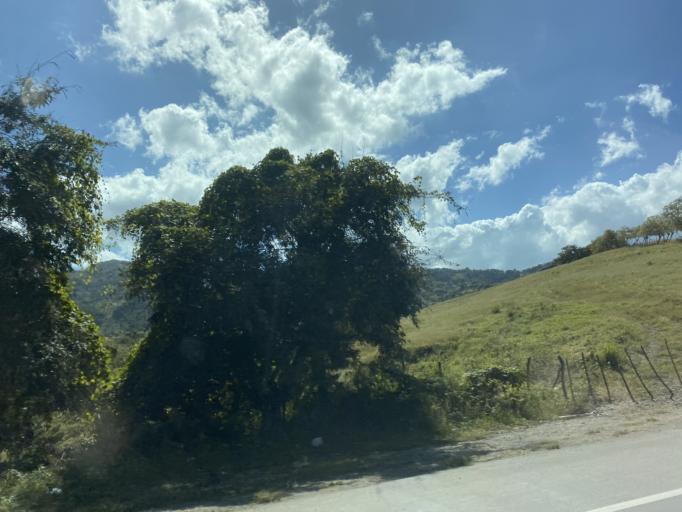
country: DO
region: Puerto Plata
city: Imbert
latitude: 19.7946
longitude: -70.8001
